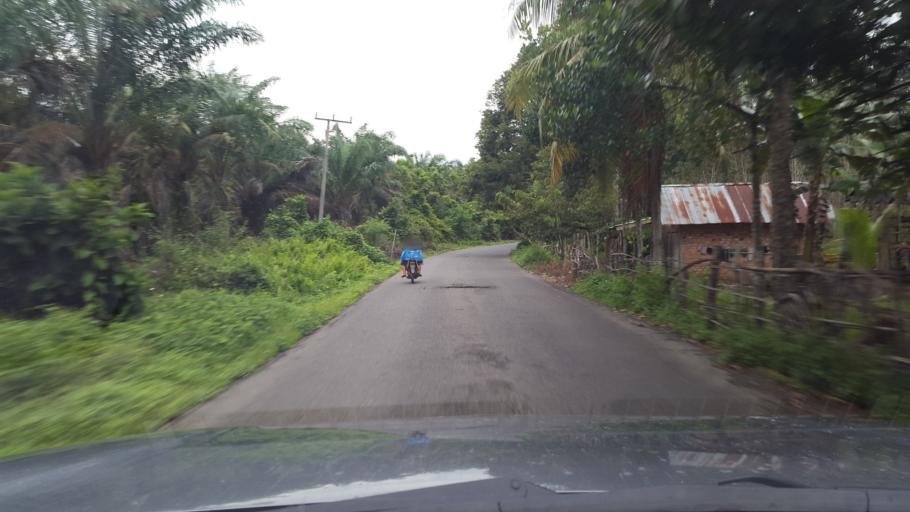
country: ID
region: South Sumatra
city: Gunungmenang
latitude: -3.1672
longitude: 103.9976
